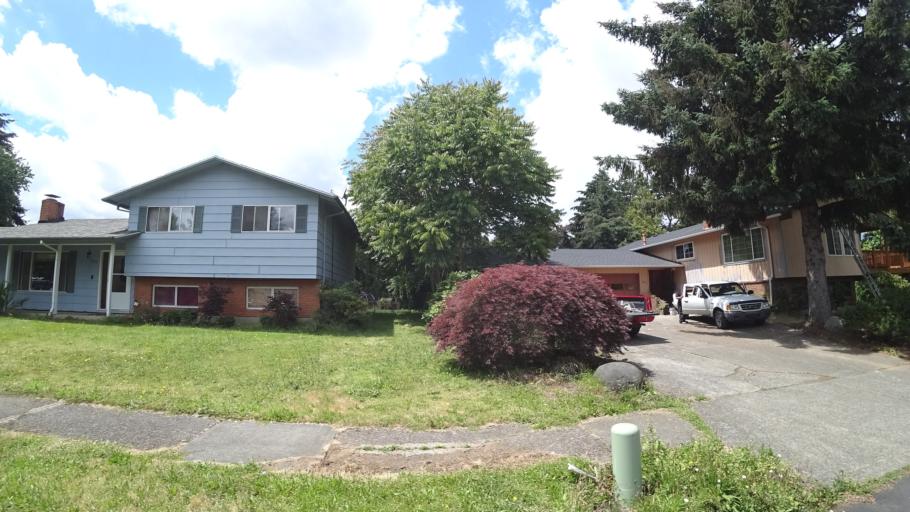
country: US
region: Oregon
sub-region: Multnomah County
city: Portland
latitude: 45.5606
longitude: -122.6070
